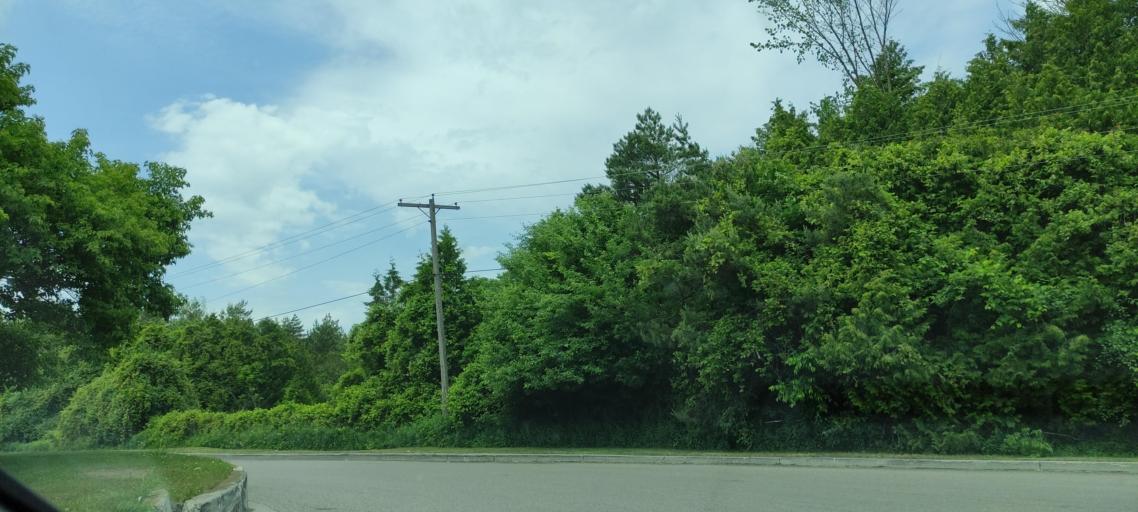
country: CA
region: Ontario
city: Oshawa
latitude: 43.9221
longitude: -78.5400
